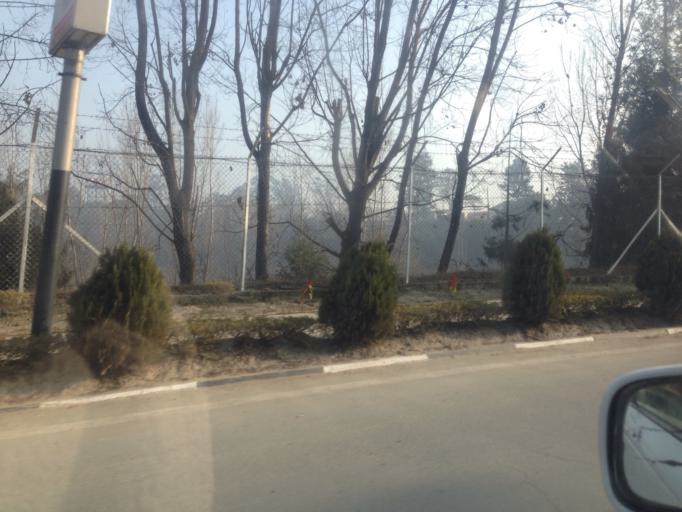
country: NP
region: Central Region
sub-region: Bagmati Zone
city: Kathmandu
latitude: 27.7013
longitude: 85.3544
